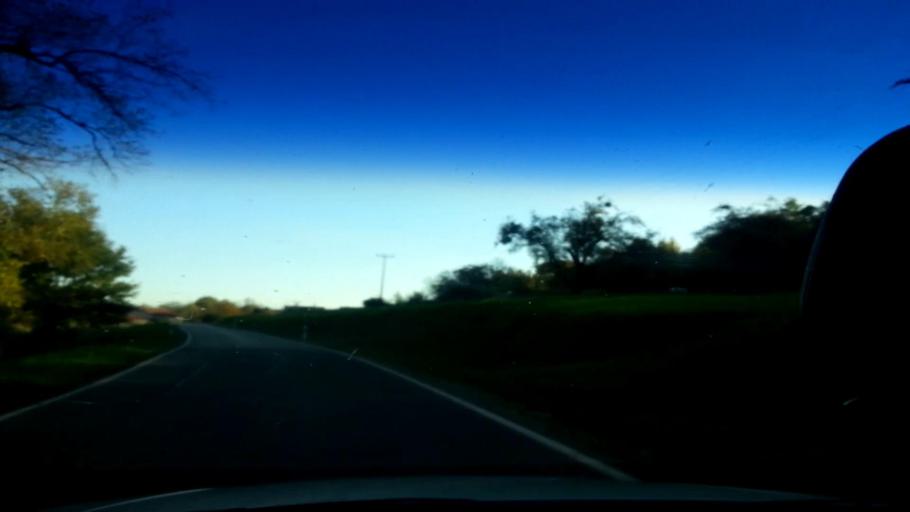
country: DE
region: Bavaria
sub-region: Upper Franconia
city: Rattelsdorf
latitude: 50.0073
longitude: 10.8731
